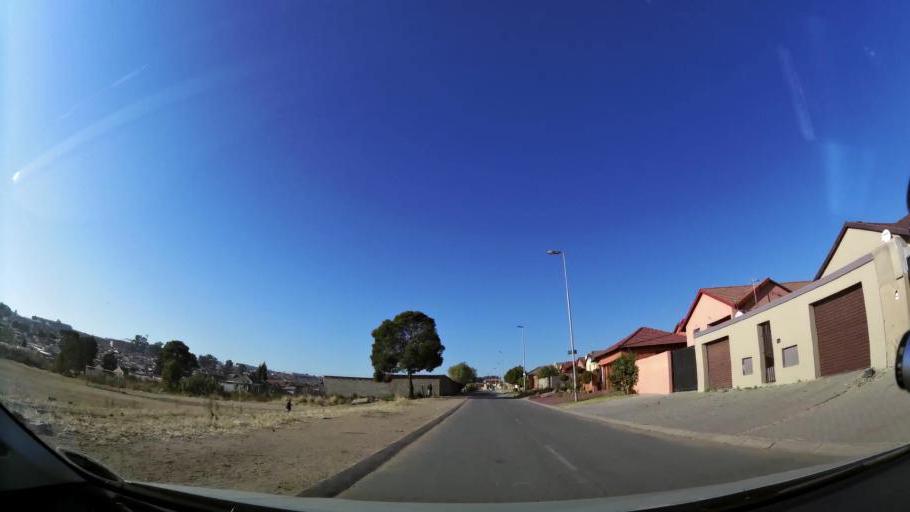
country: ZA
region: Gauteng
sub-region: City of Johannesburg Metropolitan Municipality
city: Modderfontein
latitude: -26.0446
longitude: 28.1540
